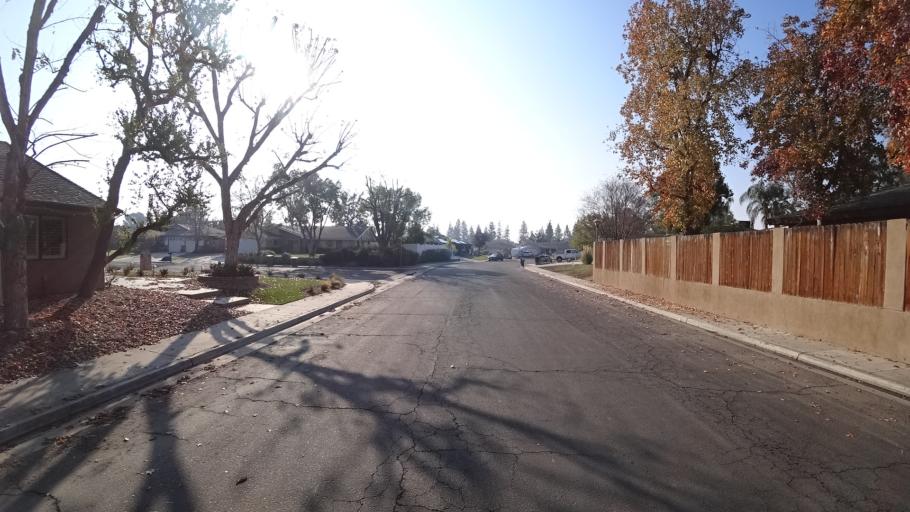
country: US
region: California
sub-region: Kern County
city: Greenacres
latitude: 35.3385
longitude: -119.0810
